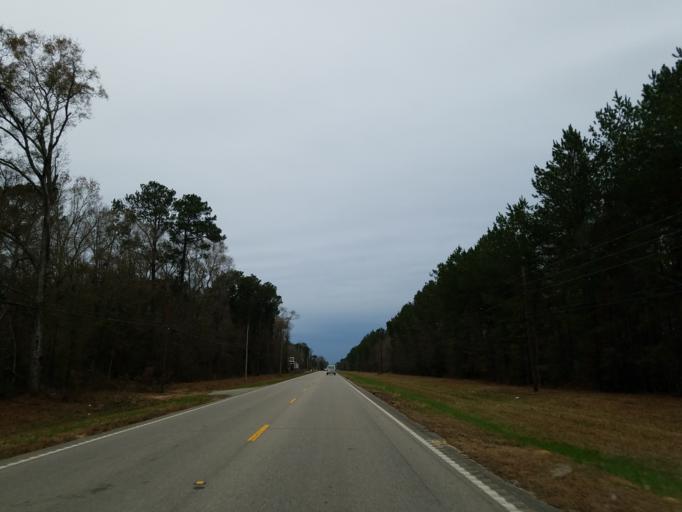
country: US
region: Mississippi
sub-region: Forrest County
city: Glendale
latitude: 31.4245
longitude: -89.2810
